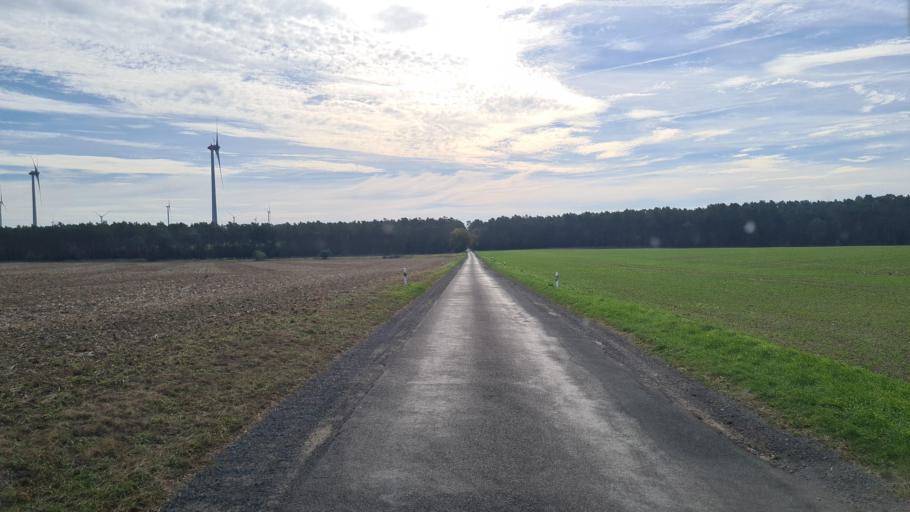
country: DE
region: Brandenburg
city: Linthe
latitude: 52.1080
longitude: 12.7521
